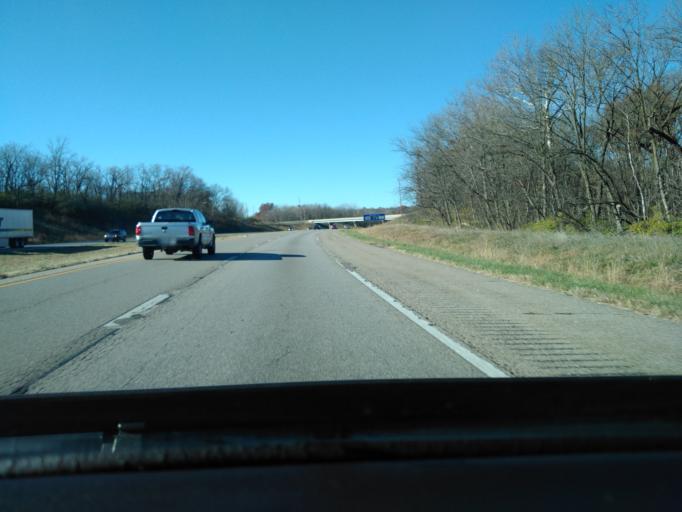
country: US
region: Illinois
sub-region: Bond County
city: Greenville
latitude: 38.8336
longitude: -89.5119
